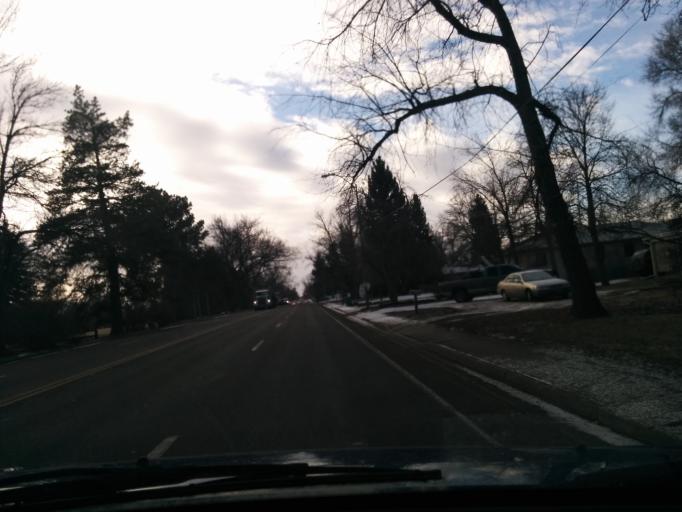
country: US
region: Colorado
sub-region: Larimer County
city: Fort Collins
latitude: 40.5855
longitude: -105.1150
